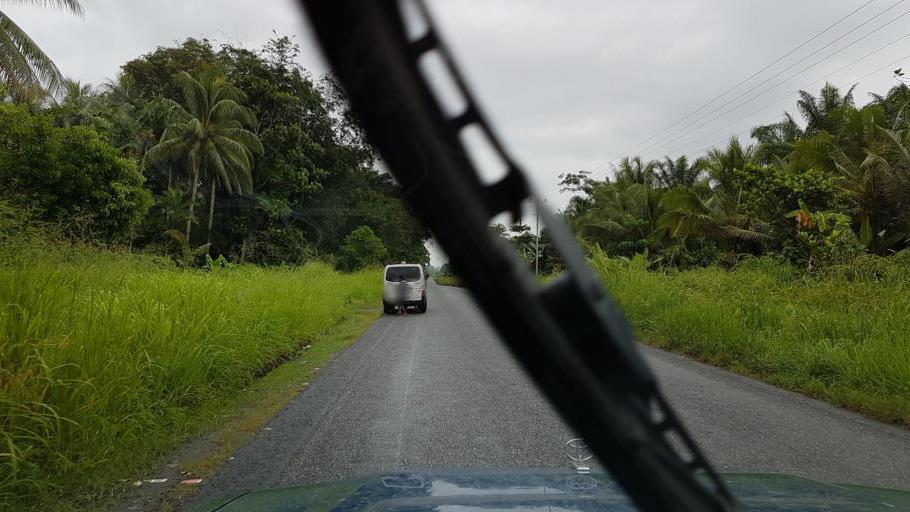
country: PG
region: Northern Province
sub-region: Sohe
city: Popondetta
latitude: -8.7872
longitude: 148.2281
